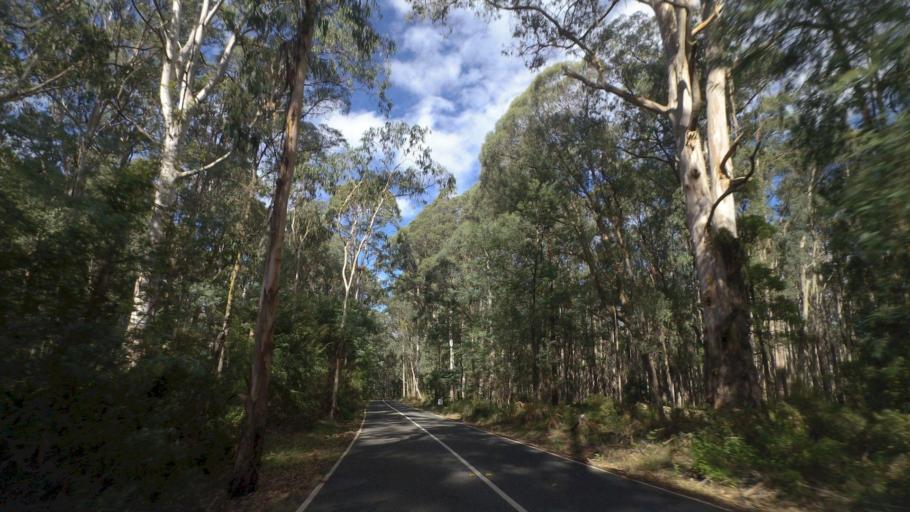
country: AU
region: Victoria
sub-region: Cardinia
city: Gembrook
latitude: -37.9829
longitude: 145.5886
